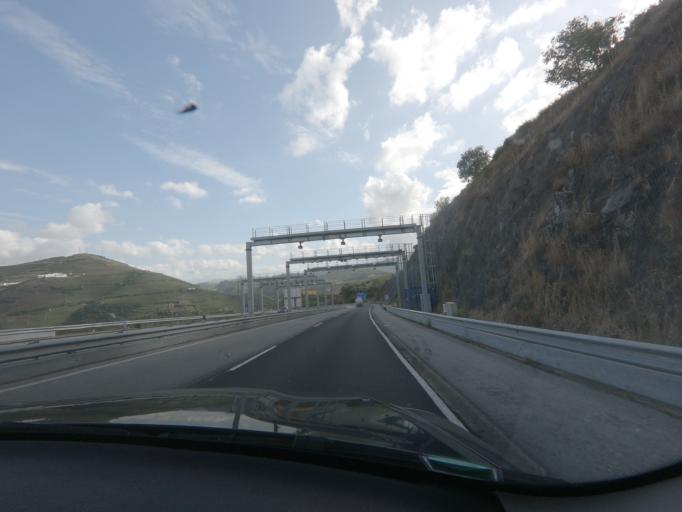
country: PT
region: Vila Real
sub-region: Peso da Regua
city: Peso da Regua
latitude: 41.1624
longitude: -7.7720
